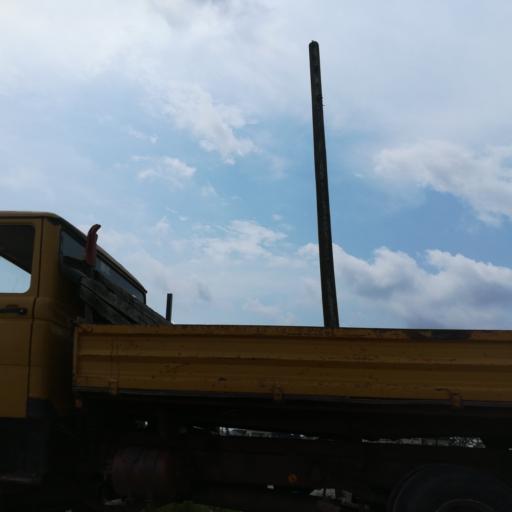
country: NG
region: Rivers
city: Port Harcourt
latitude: 4.8830
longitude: 7.0121
